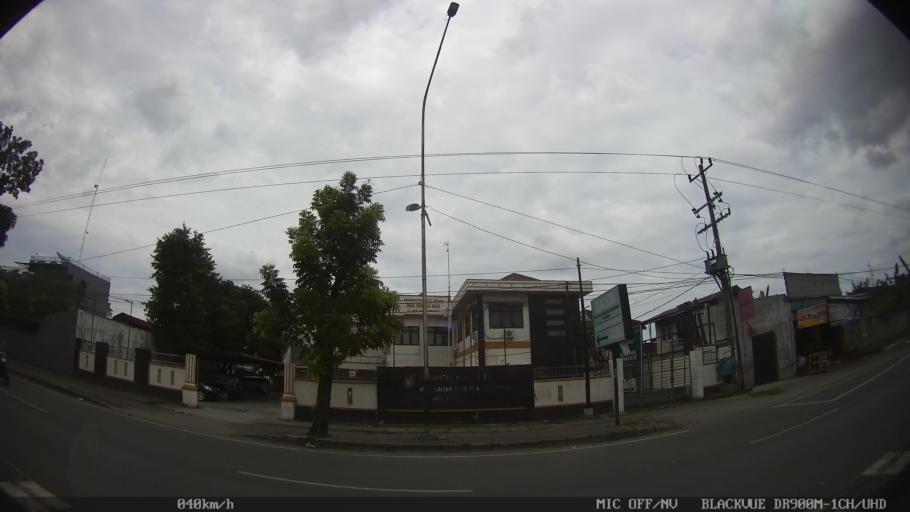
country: ID
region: North Sumatra
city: Sunggal
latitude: 3.5958
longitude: 98.6163
